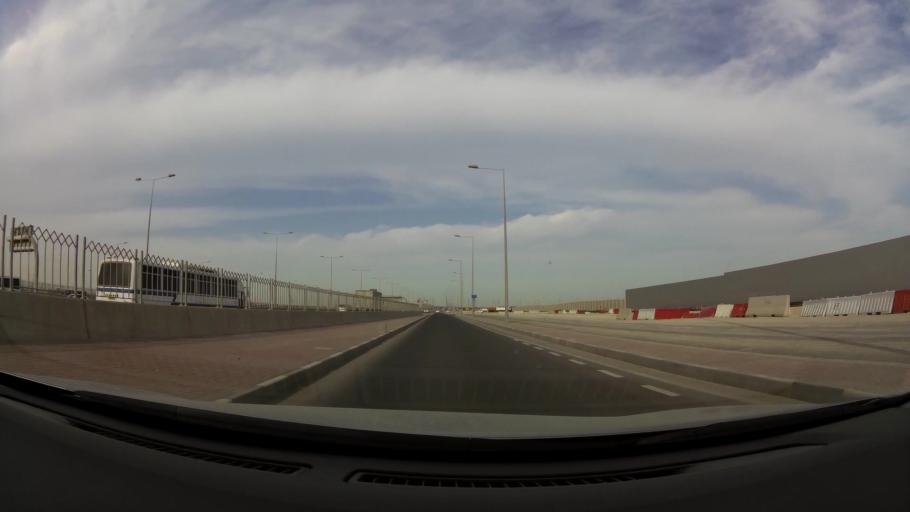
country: QA
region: Al Wakrah
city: Al Wakrah
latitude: 25.2325
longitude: 51.5792
